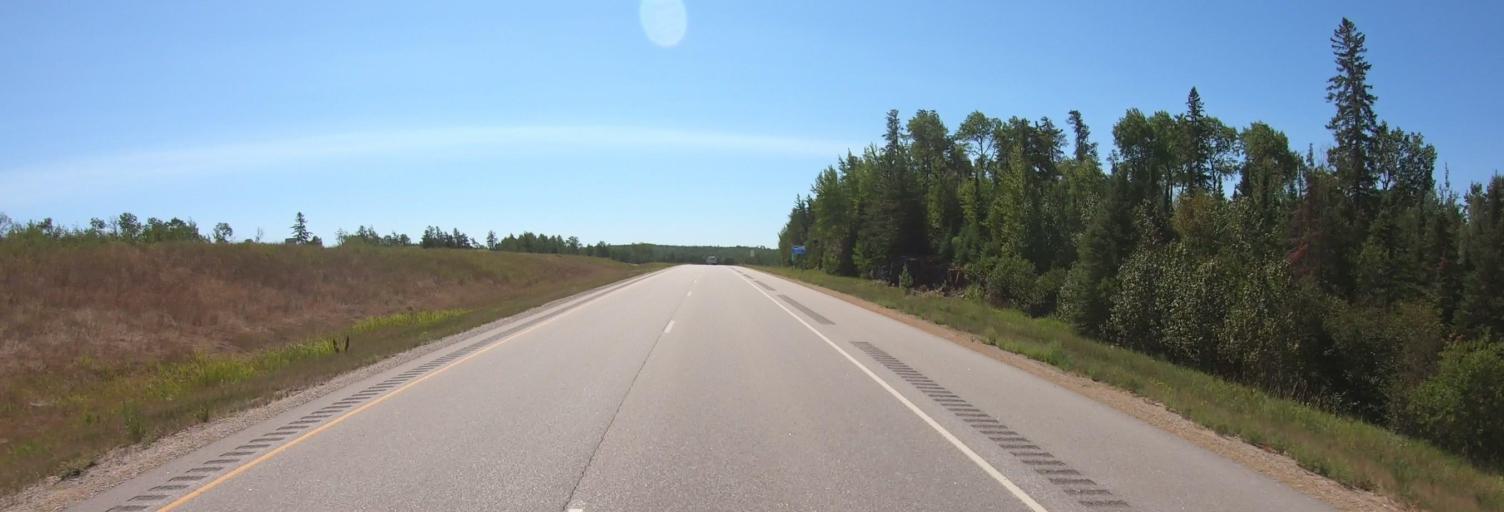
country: US
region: Minnesota
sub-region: Saint Louis County
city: Mountain Iron
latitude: 47.7504
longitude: -92.6490
